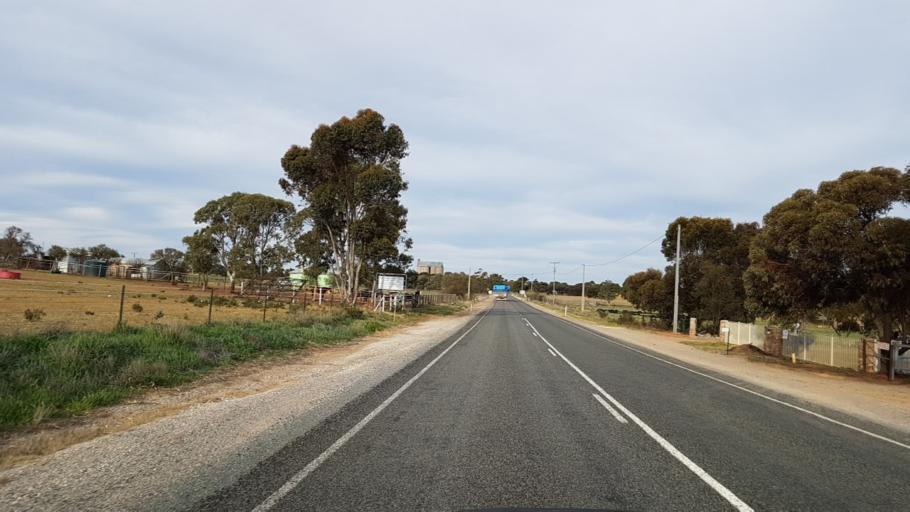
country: AU
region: South Australia
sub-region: Peterborough
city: Peterborough
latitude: -33.0300
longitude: 138.7404
